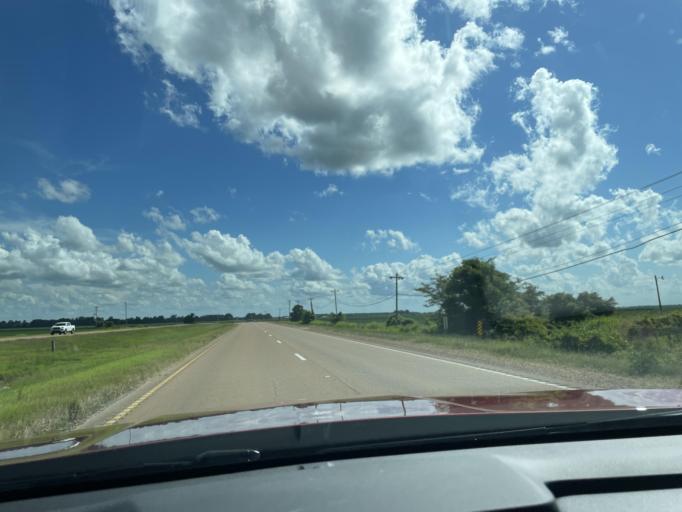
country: US
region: Mississippi
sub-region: Humphreys County
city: Belzoni
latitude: 33.1534
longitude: -90.5056
